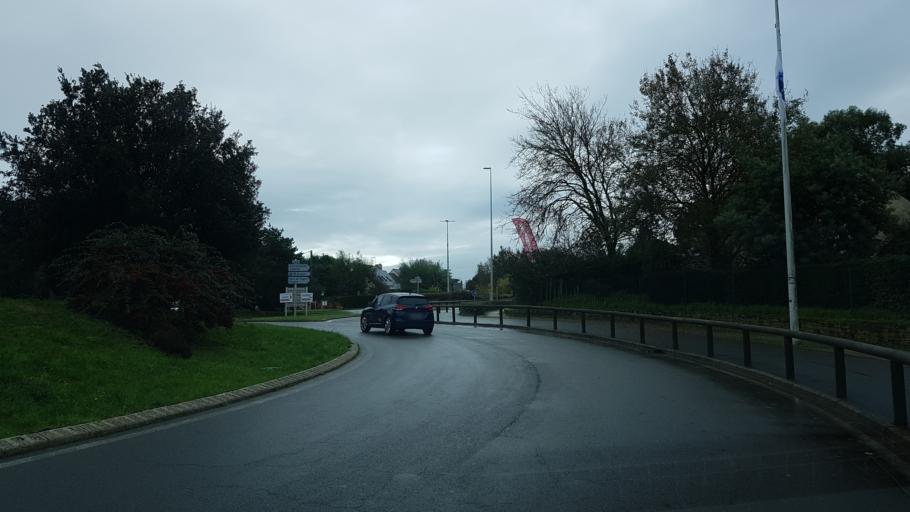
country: FR
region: Brittany
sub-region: Departement du Morbihan
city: Arzon
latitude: 47.5412
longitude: -2.8795
